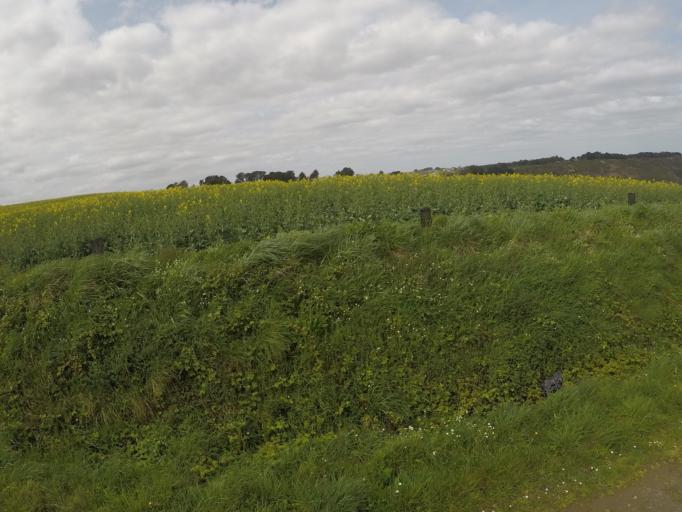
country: FR
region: Brittany
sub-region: Departement des Cotes-d'Armor
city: Plouha
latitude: 48.7189
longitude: -2.9470
